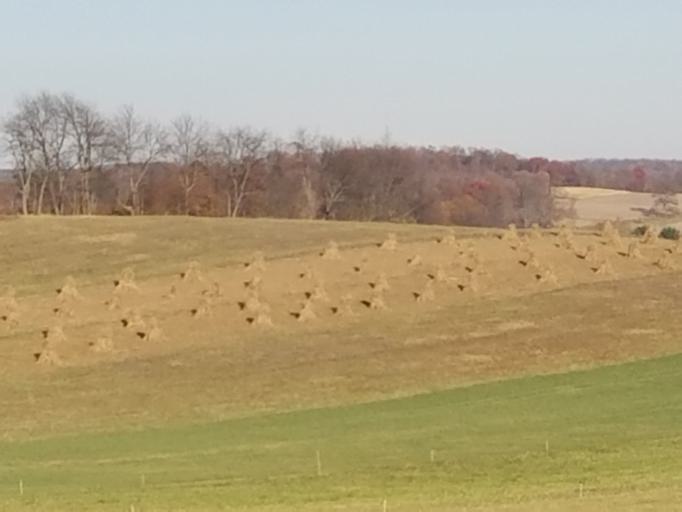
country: US
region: Ohio
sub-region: Sandusky County
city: Bellville
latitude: 40.5722
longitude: -82.3747
